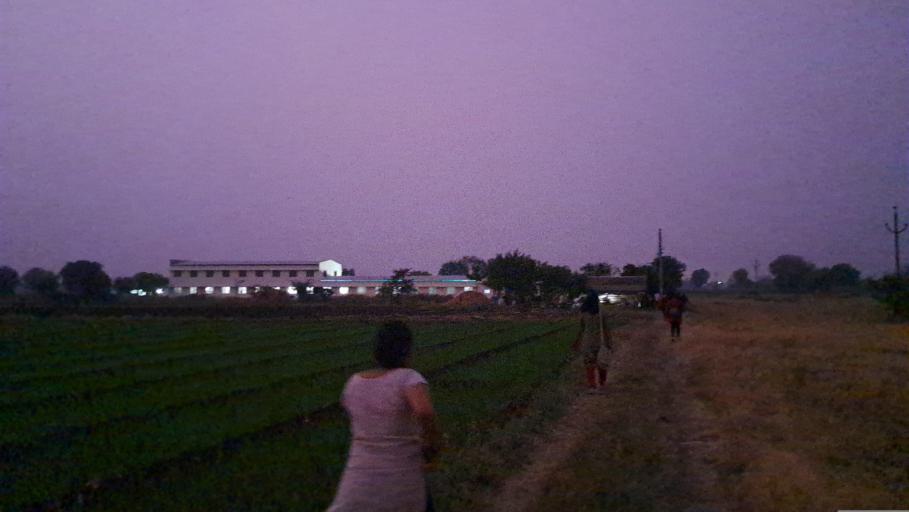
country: IN
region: Maharashtra
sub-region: Nashik Division
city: Yeola
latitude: 19.9868
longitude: 74.4908
